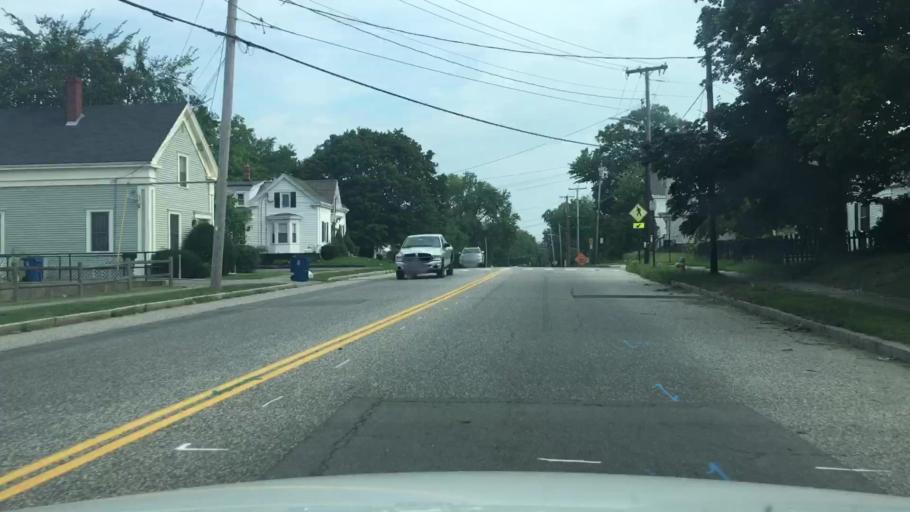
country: US
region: Maine
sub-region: Cumberland County
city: Portland
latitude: 43.6906
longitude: -70.2932
